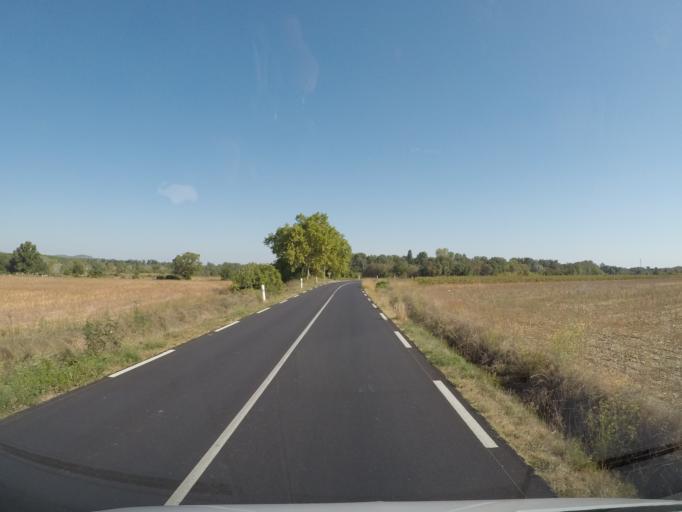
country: FR
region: Languedoc-Roussillon
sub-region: Departement du Gard
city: Lezan
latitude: 44.0209
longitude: 4.0564
